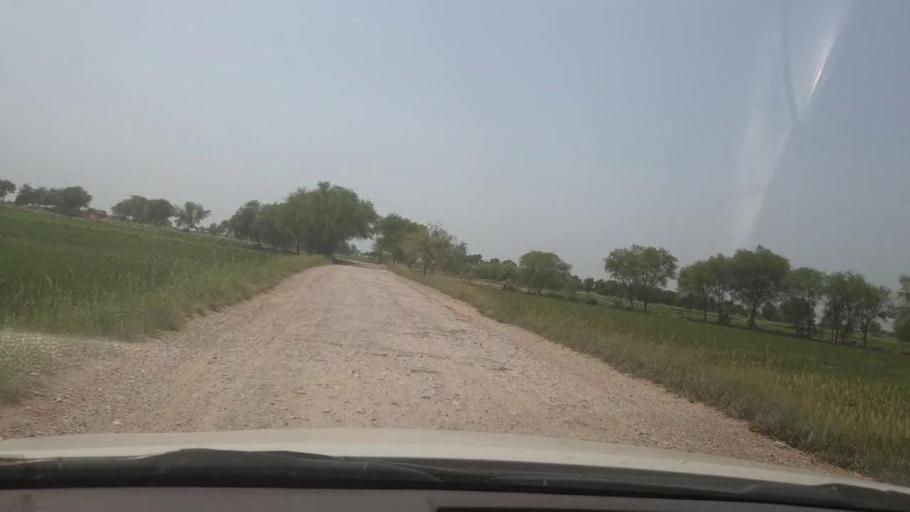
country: PK
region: Sindh
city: Shikarpur
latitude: 27.9940
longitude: 68.5803
